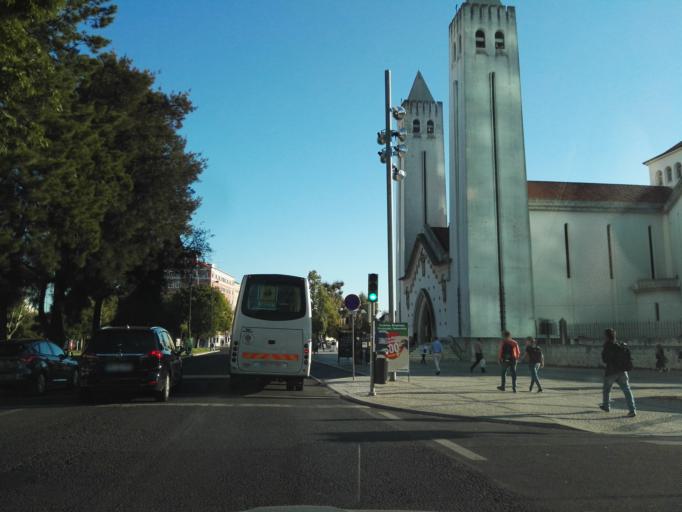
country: PT
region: Lisbon
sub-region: Lisbon
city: Lisbon
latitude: 38.7410
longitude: -9.1377
